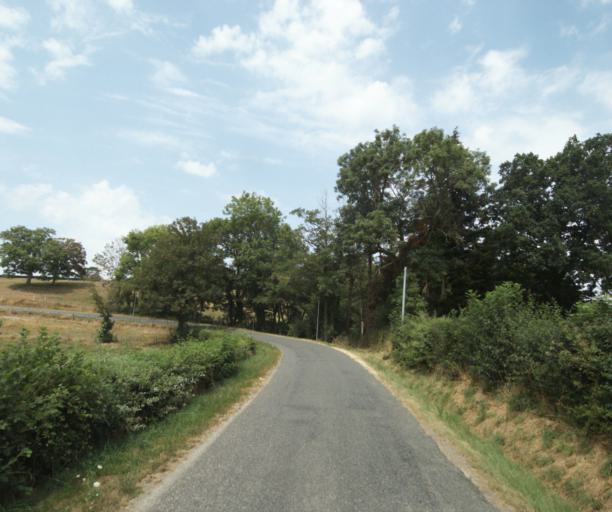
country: FR
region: Bourgogne
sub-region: Departement de Saone-et-Loire
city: Gueugnon
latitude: 46.6025
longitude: 4.0114
